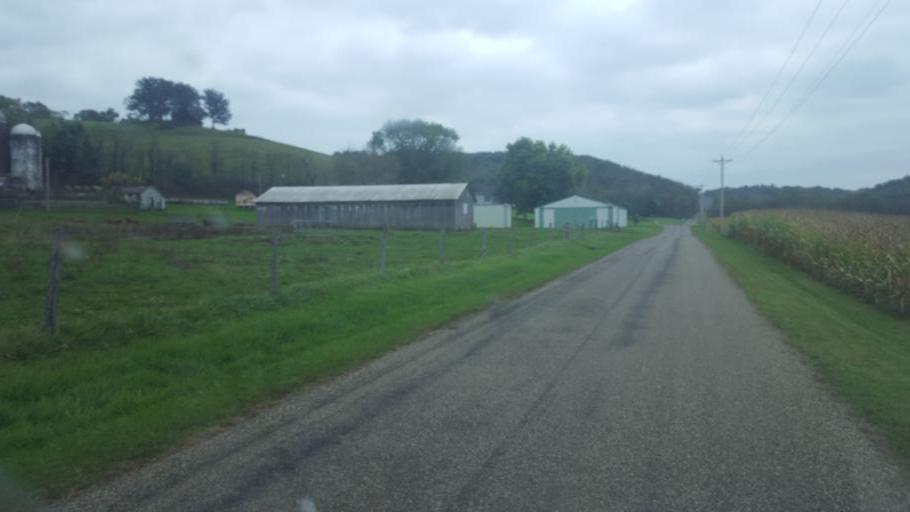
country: US
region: Ohio
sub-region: Carroll County
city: Carrollton
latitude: 40.4305
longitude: -81.0247
